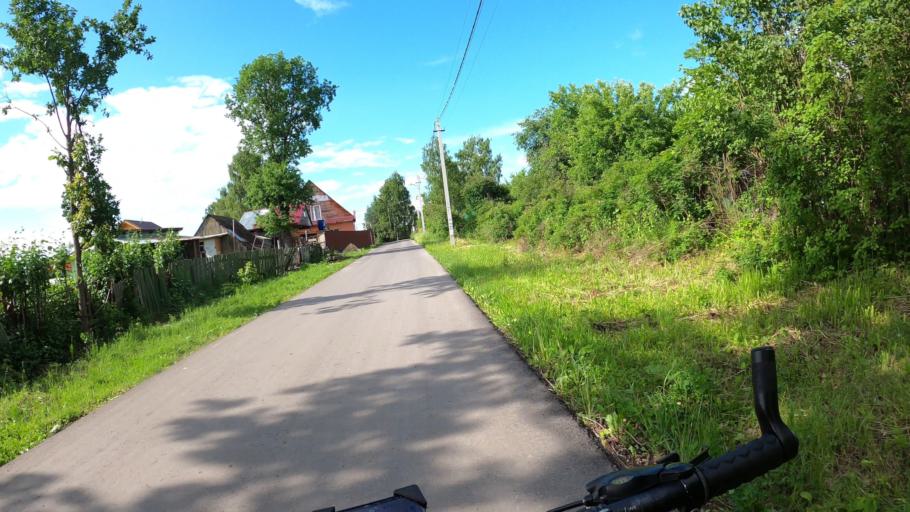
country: RU
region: Moskovskaya
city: Konobeyevo
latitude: 55.4234
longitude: 38.6503
